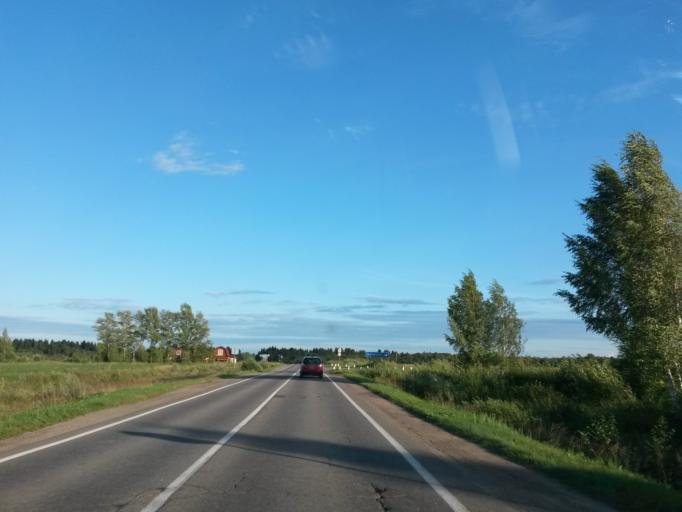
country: RU
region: Jaroslavl
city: Yaroslavl
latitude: 57.7910
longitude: 39.8306
